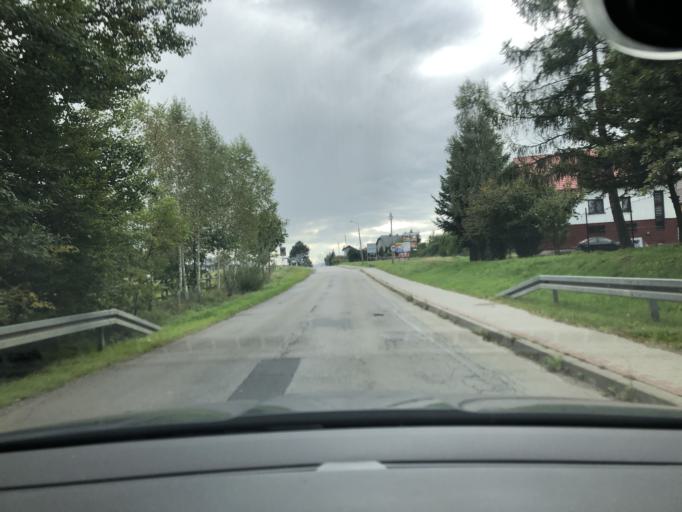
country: PL
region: Silesian Voivodeship
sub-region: Powiat zywiecki
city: Zarzecze
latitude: 49.7221
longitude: 19.1776
